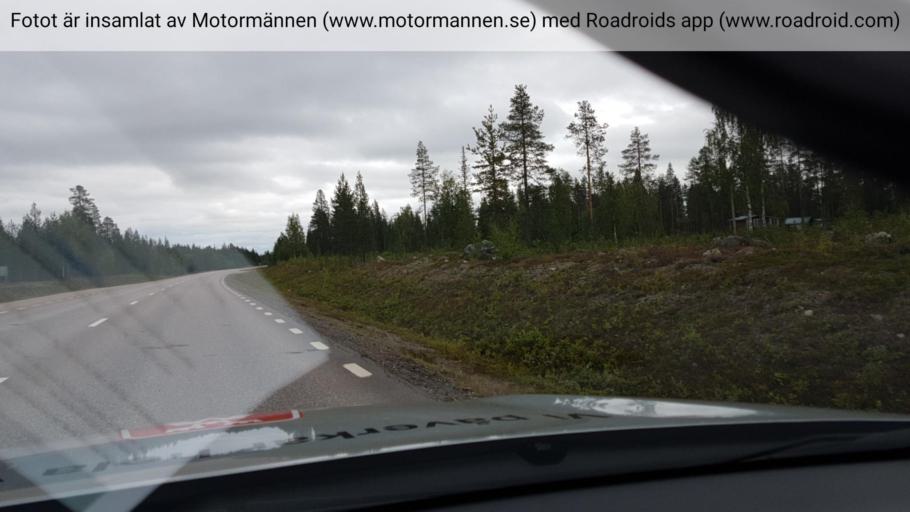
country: SE
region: Norrbotten
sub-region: Gallivare Kommun
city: Gaellivare
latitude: 67.0756
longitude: 21.0892
